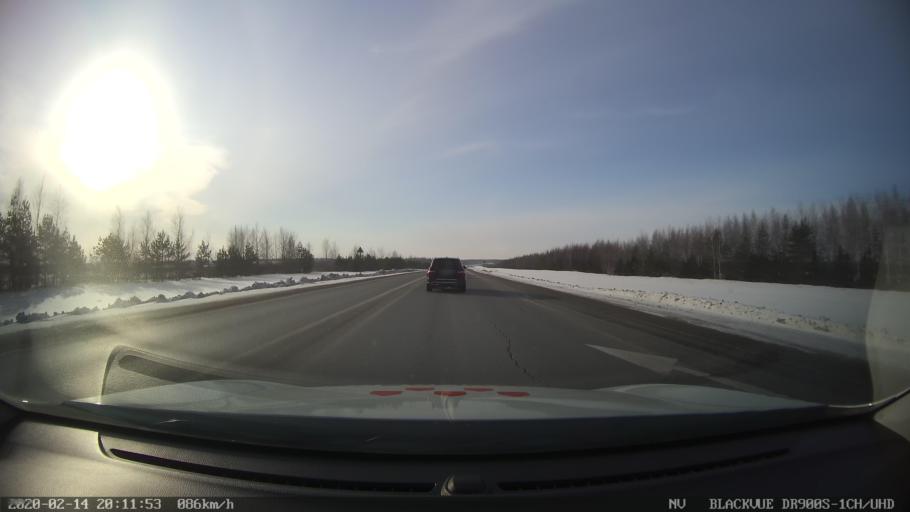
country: RU
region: Tatarstan
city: Verkhniy Uslon
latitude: 55.6721
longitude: 48.8684
